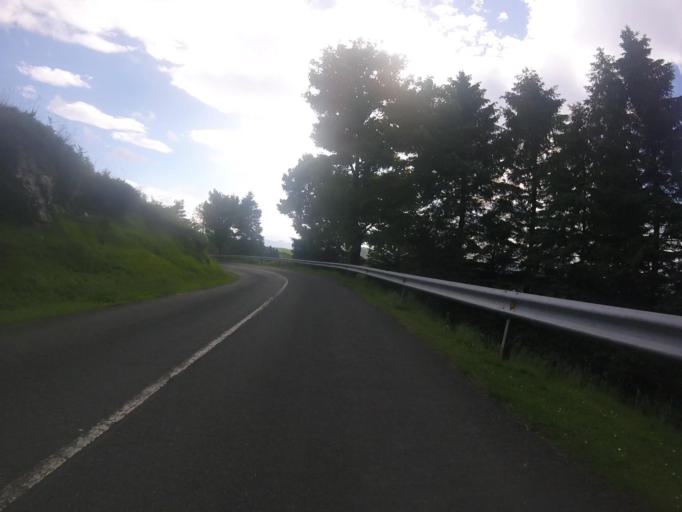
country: ES
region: Navarre
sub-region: Provincia de Navarra
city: Goizueta
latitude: 43.2451
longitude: -1.8261
